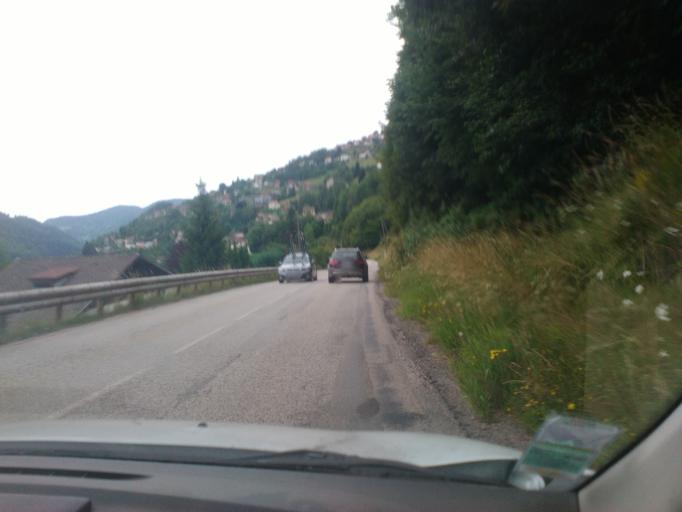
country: FR
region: Lorraine
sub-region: Departement des Vosges
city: La Bresse
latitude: 48.0113
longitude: 6.8803
